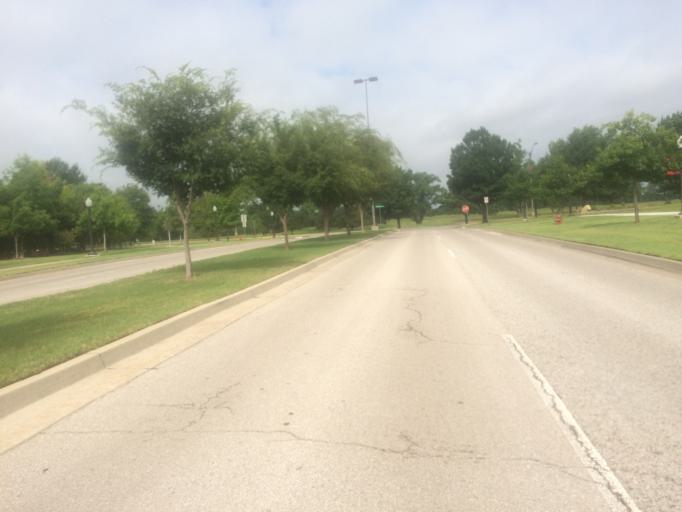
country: US
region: Oklahoma
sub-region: Cleveland County
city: Norman
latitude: 35.1831
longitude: -97.4403
